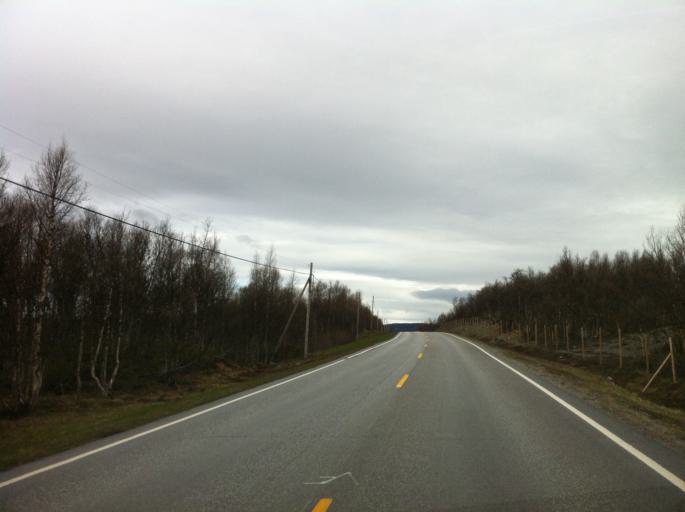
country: NO
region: Sor-Trondelag
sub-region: Tydal
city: Aas
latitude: 62.6361
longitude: 11.9231
